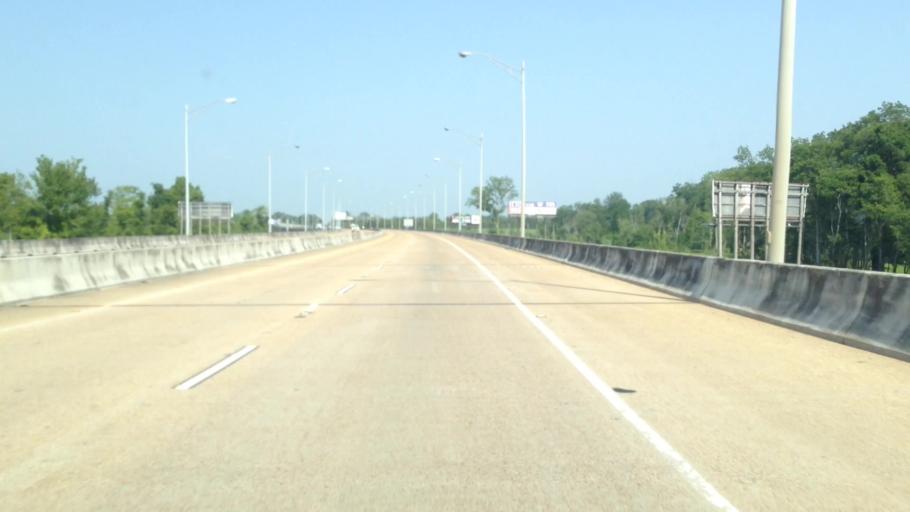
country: US
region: Mississippi
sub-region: Warren County
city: Vicksburg
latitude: 32.3187
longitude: -90.9155
